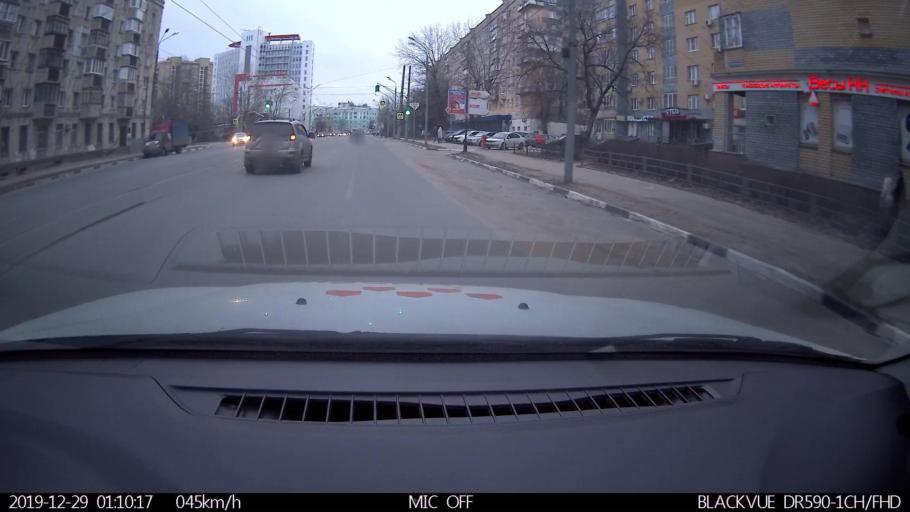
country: RU
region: Nizjnij Novgorod
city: Nizhniy Novgorod
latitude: 56.3040
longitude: 43.9379
